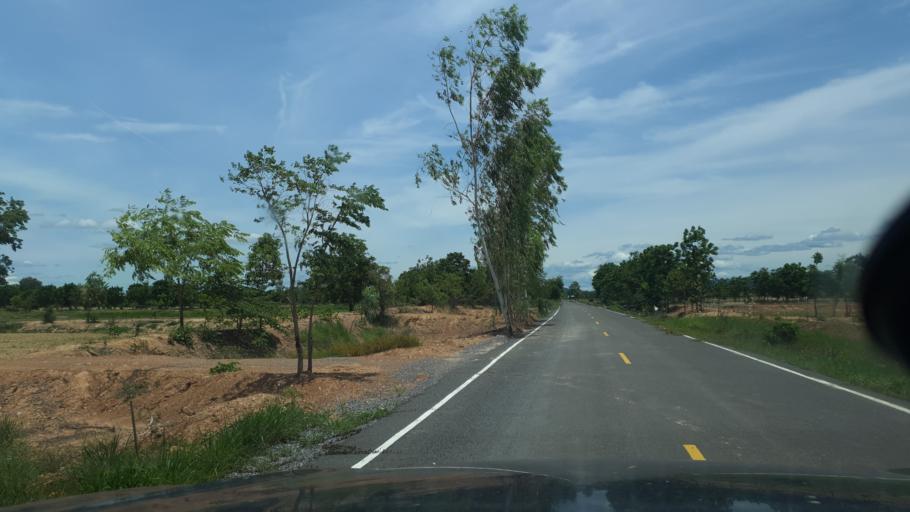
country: TH
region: Sukhothai
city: Ban Na
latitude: 17.1505
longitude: 99.6457
